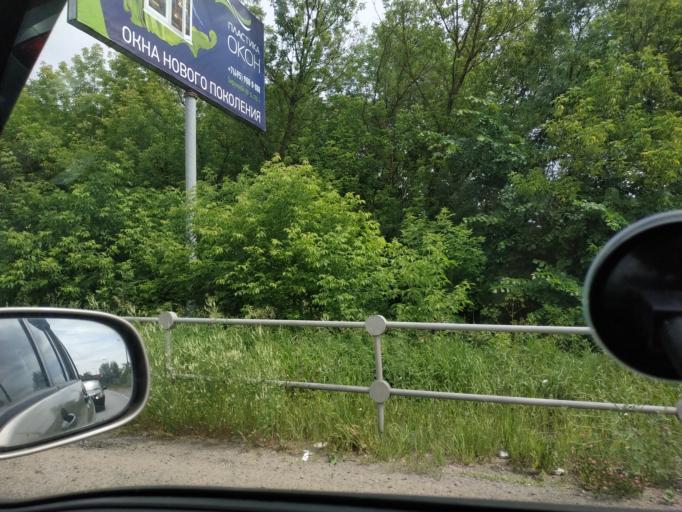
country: RU
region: Moskovskaya
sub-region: Shchelkovskiy Rayon
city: Grebnevo
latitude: 55.9644
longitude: 38.0809
